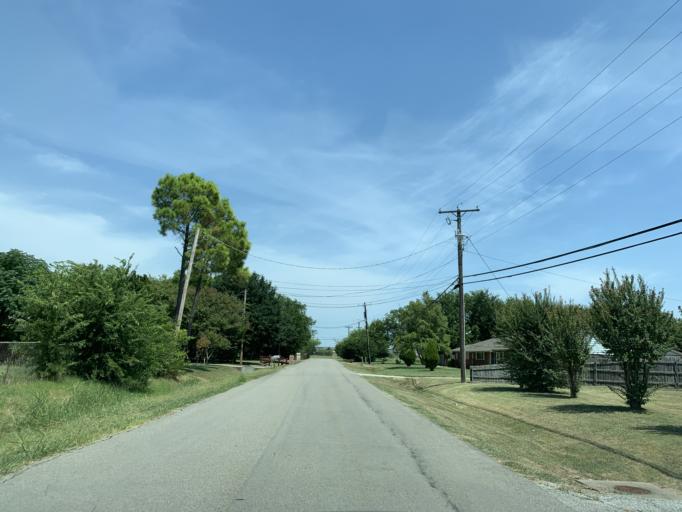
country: US
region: Texas
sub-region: Dallas County
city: Cedar Hill
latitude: 32.6474
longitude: -97.0164
